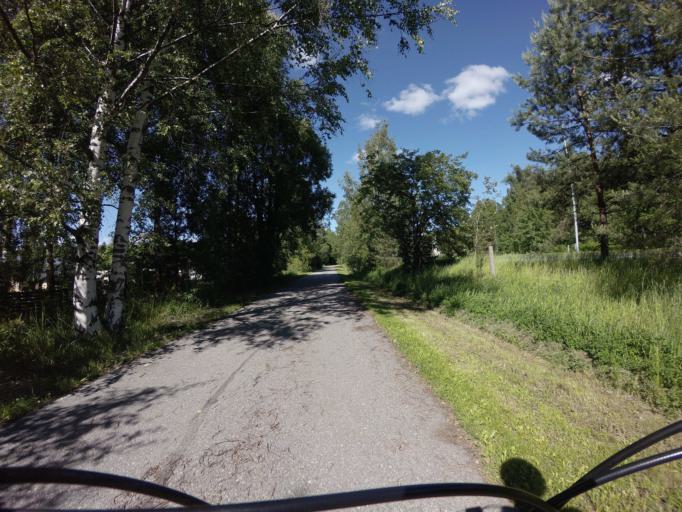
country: FI
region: Varsinais-Suomi
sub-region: Turku
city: Turku
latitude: 60.4852
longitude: 22.2747
